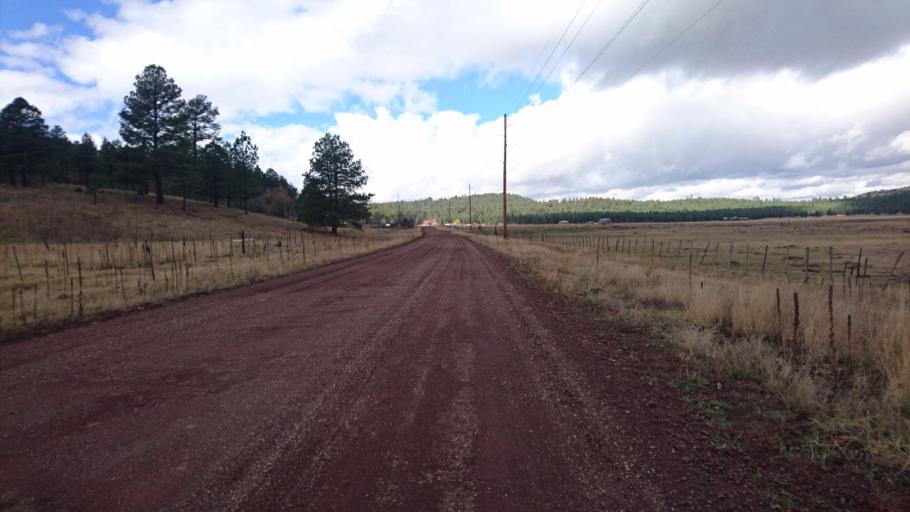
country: US
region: Arizona
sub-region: Coconino County
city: Parks
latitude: 35.2696
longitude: -111.8861
